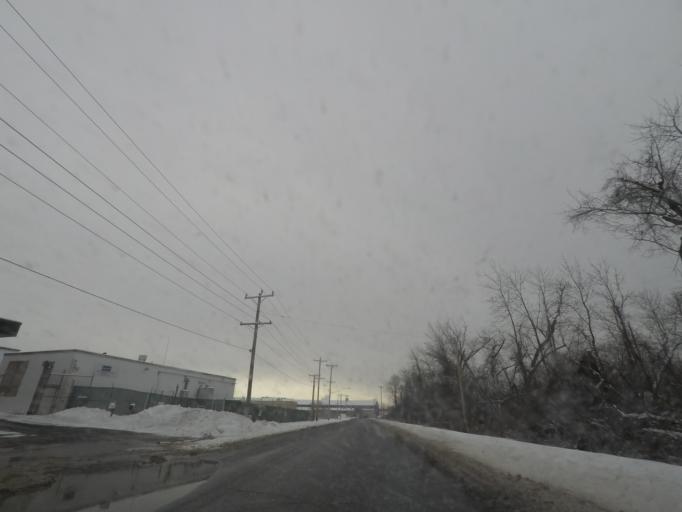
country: US
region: New York
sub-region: Rensselaer County
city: Rensselaer
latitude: 42.6170
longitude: -73.7641
